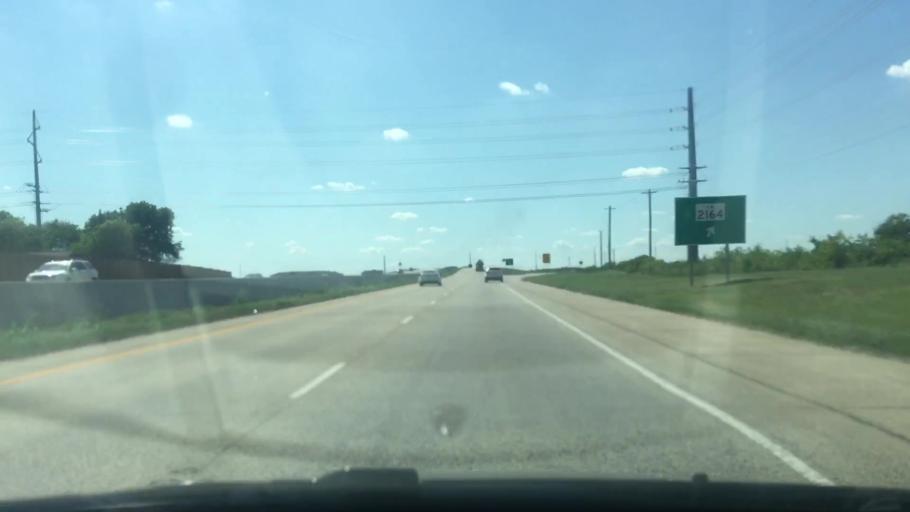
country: US
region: Texas
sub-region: Denton County
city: Denton
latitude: 33.2604
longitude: -97.1255
